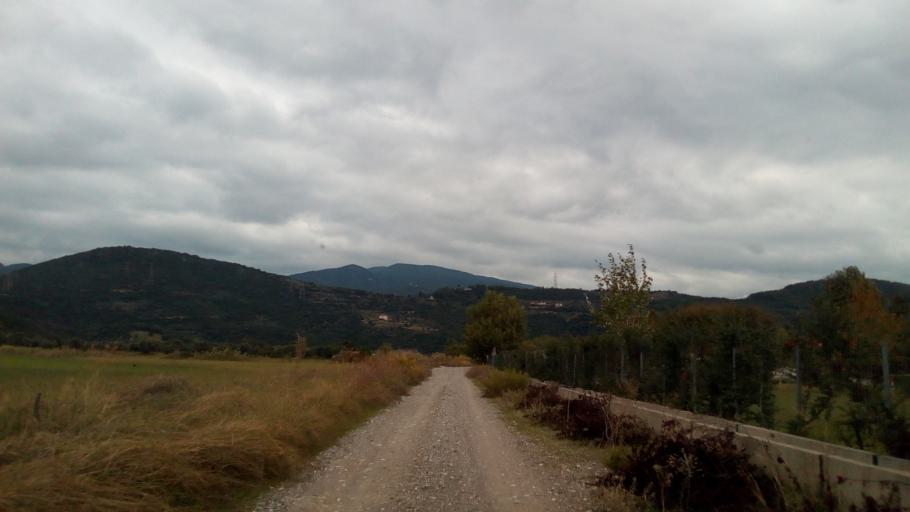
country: GR
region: West Greece
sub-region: Nomos Aitolias kai Akarnanias
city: Nafpaktos
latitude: 38.3986
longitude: 21.9181
